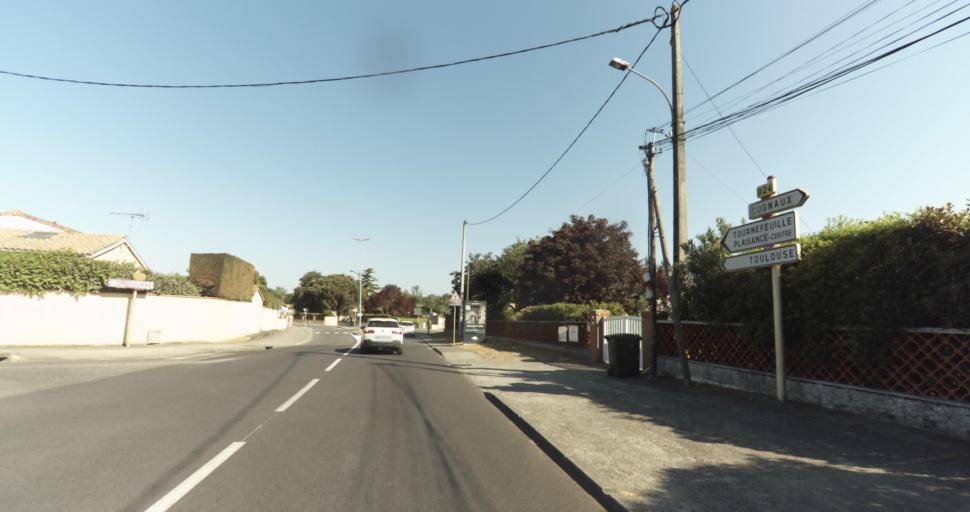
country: FR
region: Midi-Pyrenees
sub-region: Departement de la Haute-Garonne
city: Plaisance-du-Touch
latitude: 43.5599
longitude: 1.3014
